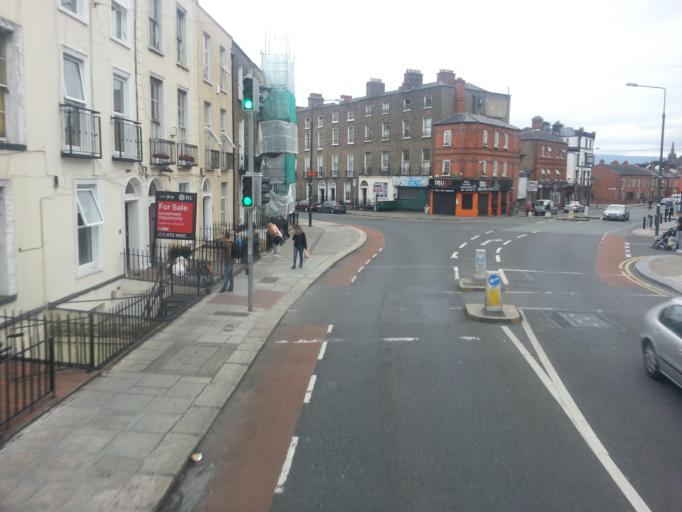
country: IE
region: Leinster
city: Drumcondra
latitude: 53.3571
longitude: -6.2680
